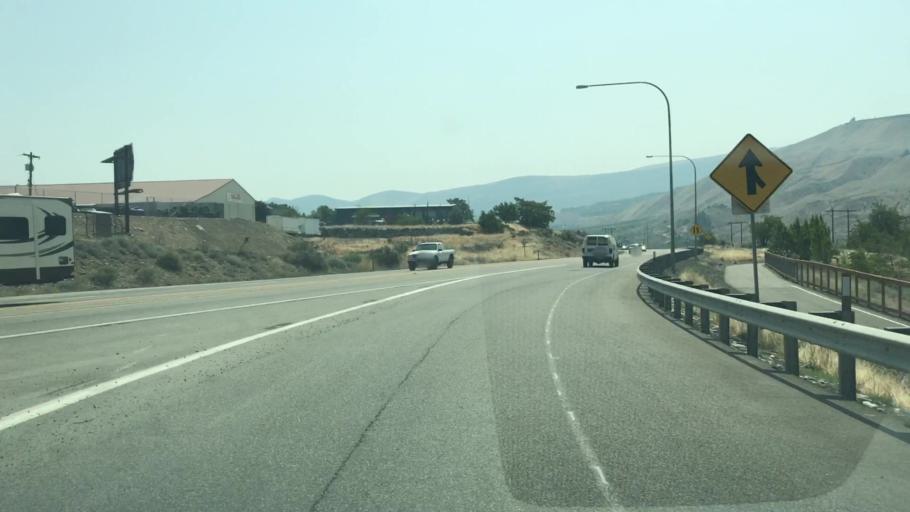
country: US
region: Washington
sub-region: Chelan County
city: South Wenatchee
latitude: 47.3984
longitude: -120.2867
